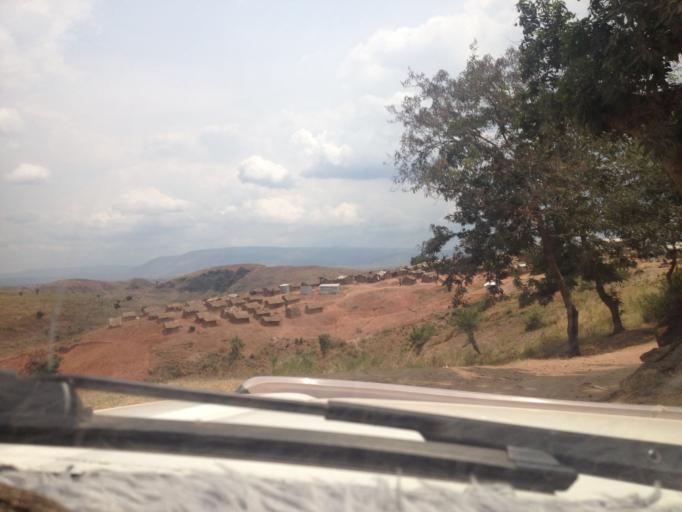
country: CD
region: Katanga
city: Kalemie
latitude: -5.9294
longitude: 29.1741
